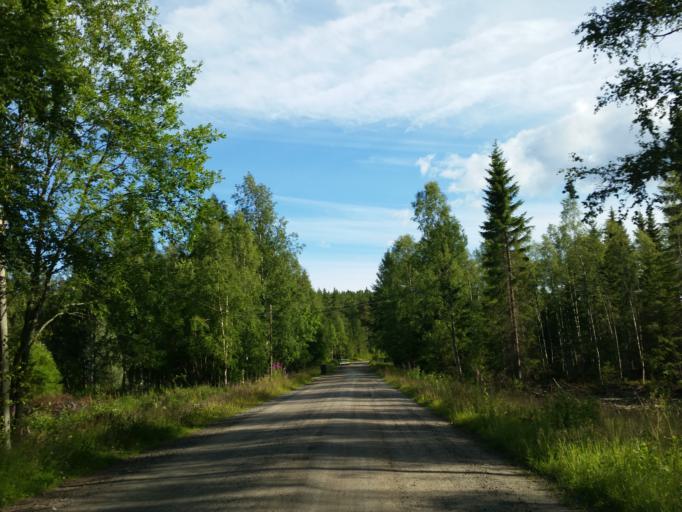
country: SE
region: Vaesterbotten
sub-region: Robertsfors Kommun
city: Robertsfors
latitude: 64.0385
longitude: 20.8508
